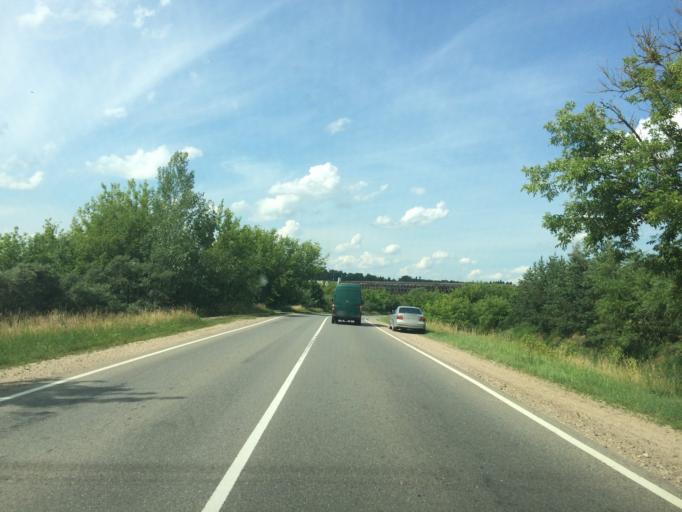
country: LT
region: Kauno apskritis
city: Jonava
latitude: 55.0720
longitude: 24.2939
